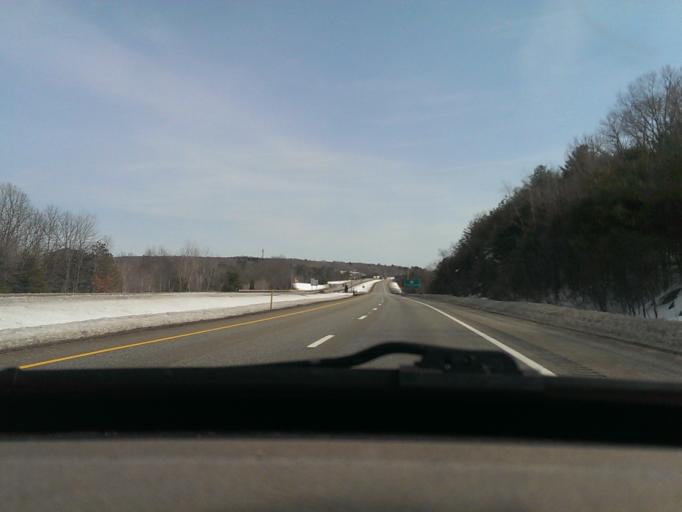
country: US
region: Massachusetts
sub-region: Worcester County
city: Millville
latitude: 42.0286
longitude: -71.6141
